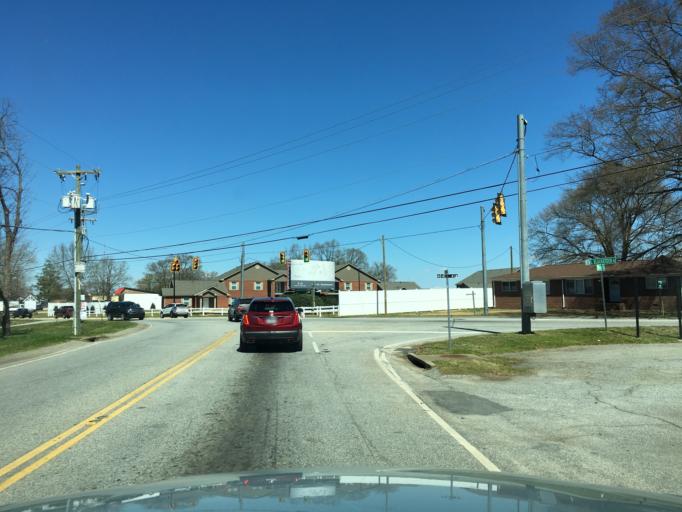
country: US
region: South Carolina
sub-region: Spartanburg County
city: Fairforest
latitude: 34.9308
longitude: -82.0009
